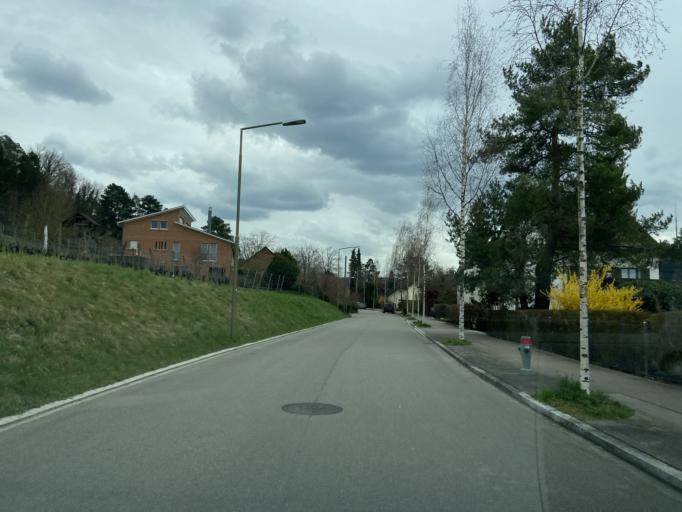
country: CH
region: Zurich
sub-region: Bezirk Winterthur
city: Wuelflingen (Kreis 6) / Lindenplatz
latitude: 47.5137
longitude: 8.7013
